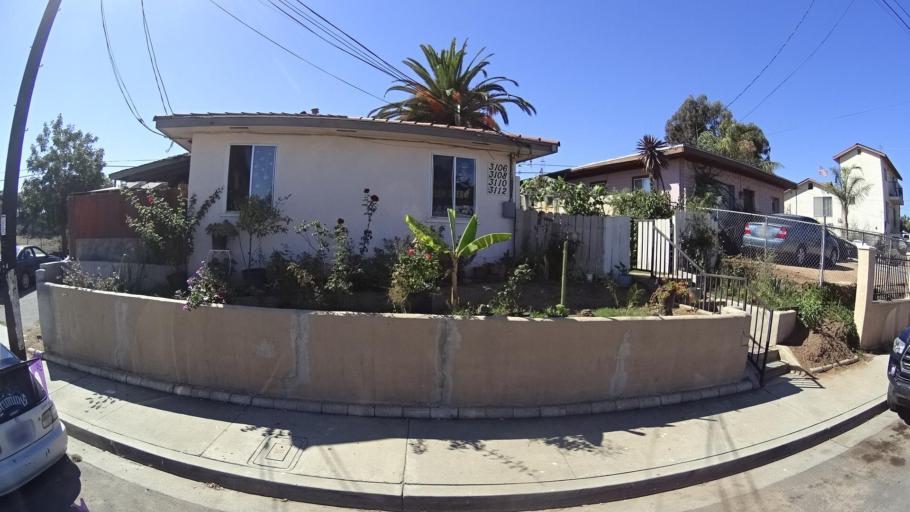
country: US
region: California
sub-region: San Diego County
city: Chula Vista
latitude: 32.6640
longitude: -117.0702
